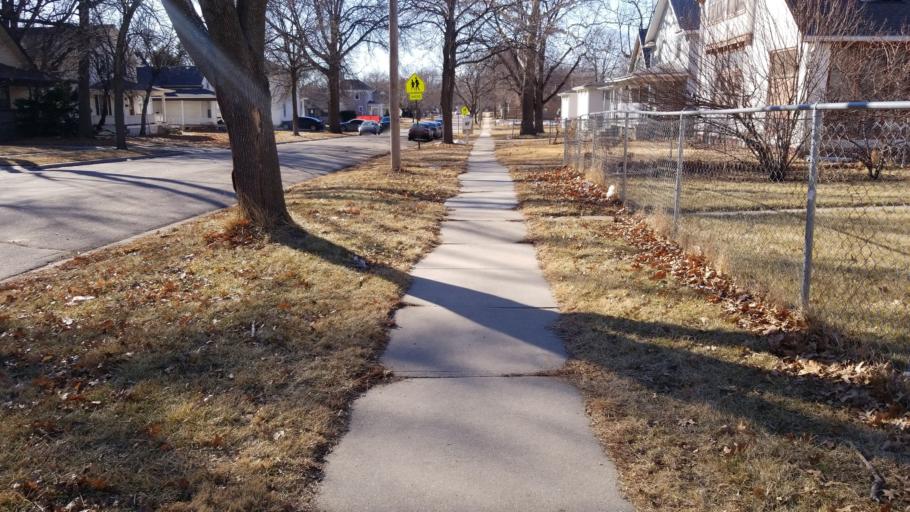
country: US
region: Nebraska
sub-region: Lancaster County
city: Lincoln
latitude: 40.8182
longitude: -96.6732
